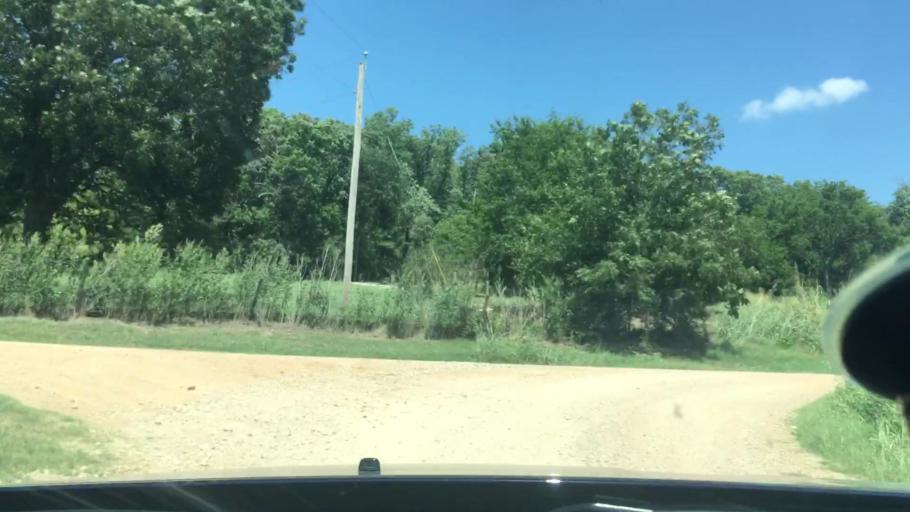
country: US
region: Oklahoma
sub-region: Johnston County
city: Tishomingo
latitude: 34.3638
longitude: -96.4421
